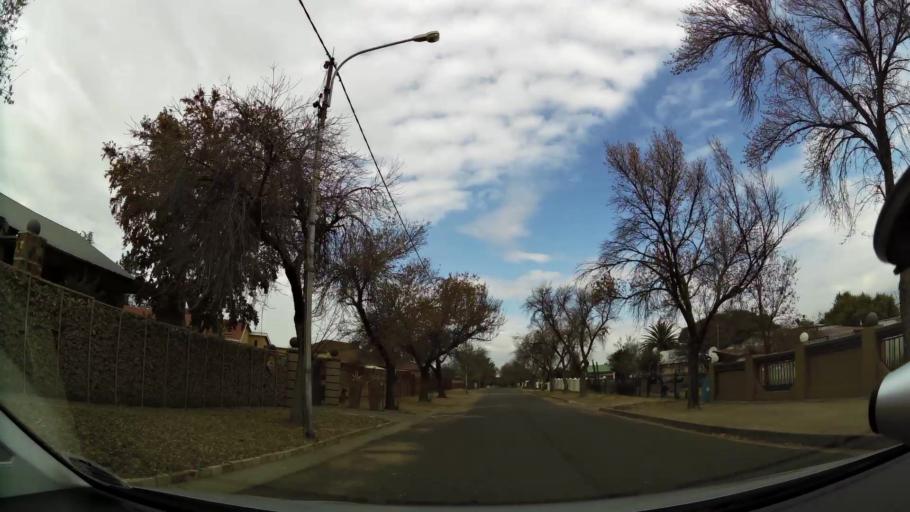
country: ZA
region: Orange Free State
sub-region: Fezile Dabi District Municipality
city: Kroonstad
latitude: -27.6372
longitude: 27.2298
